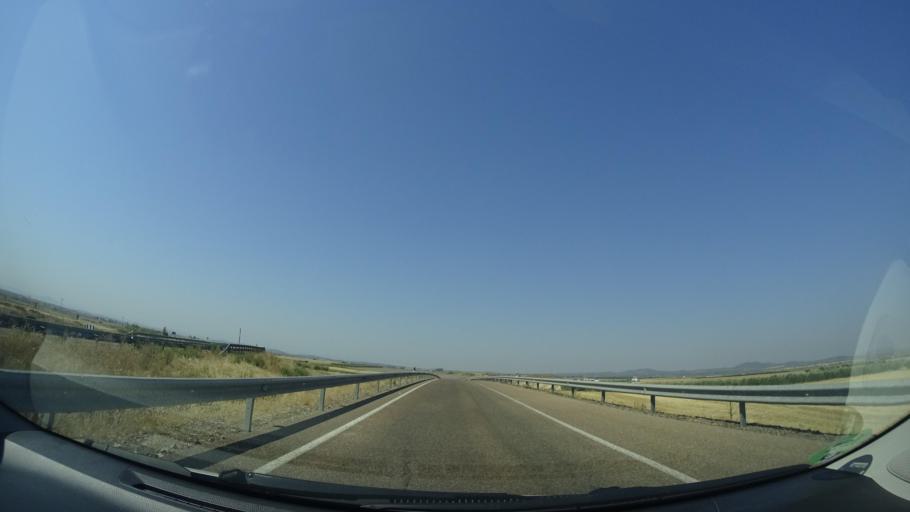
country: ES
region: Extremadura
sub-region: Provincia de Caceres
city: Miajadas
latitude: 39.1272
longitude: -5.9572
